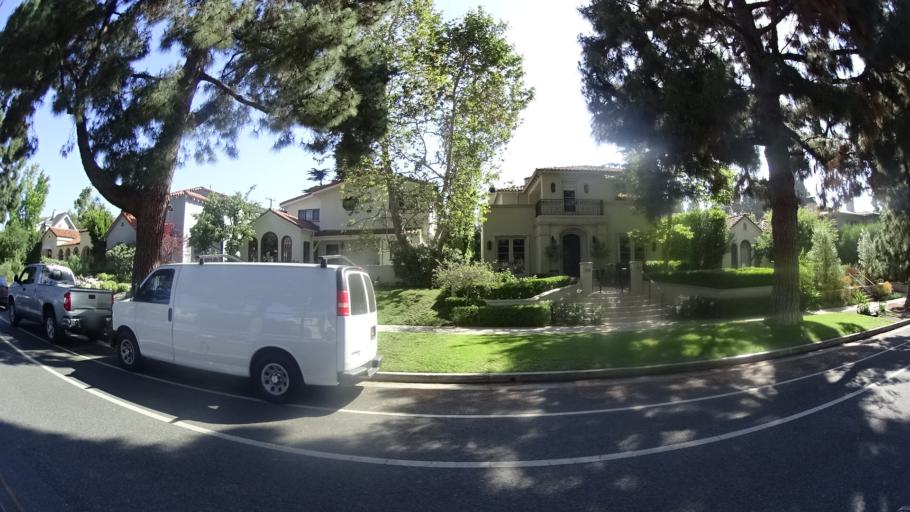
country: US
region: California
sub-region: Los Angeles County
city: Santa Monica
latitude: 34.0370
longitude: -118.5009
